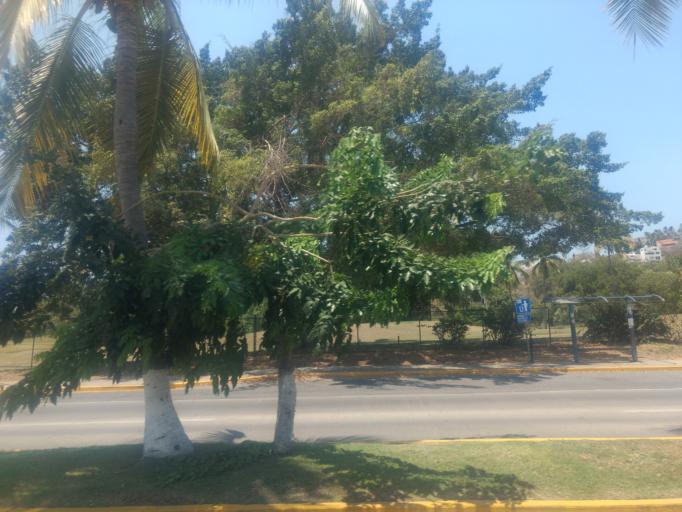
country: MX
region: Colima
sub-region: Manzanillo
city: Manzanillo
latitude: 19.1138
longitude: -104.3433
